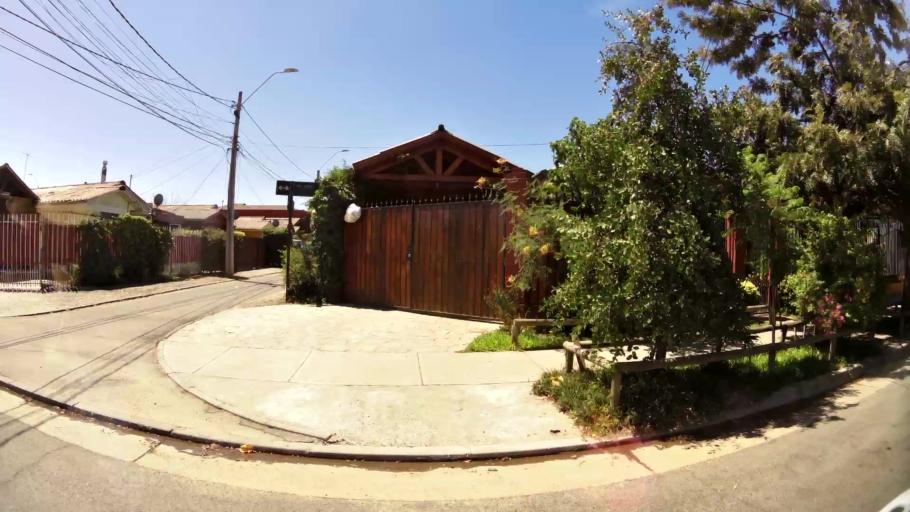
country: CL
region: O'Higgins
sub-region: Provincia de Cachapoal
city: Rancagua
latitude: -34.1672
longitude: -70.7788
